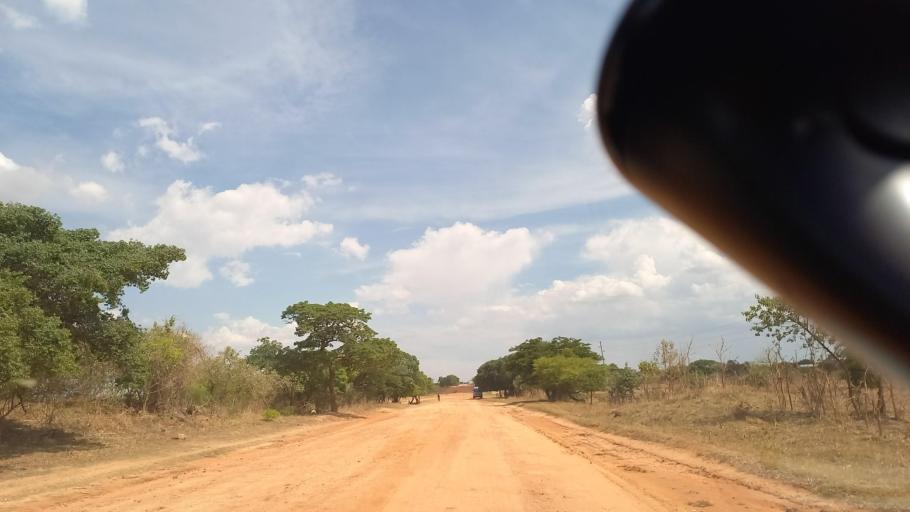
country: ZM
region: Lusaka
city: Kafue
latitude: -16.1333
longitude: 28.0491
